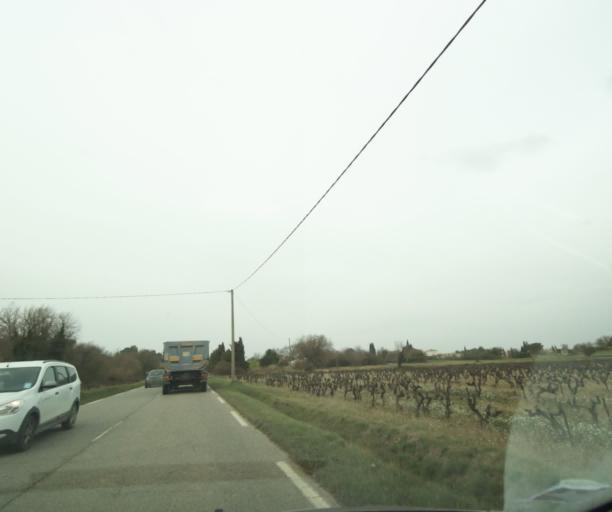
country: FR
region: Provence-Alpes-Cote d'Azur
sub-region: Departement des Bouches-du-Rhone
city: Peynier
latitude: 43.4468
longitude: 5.6518
